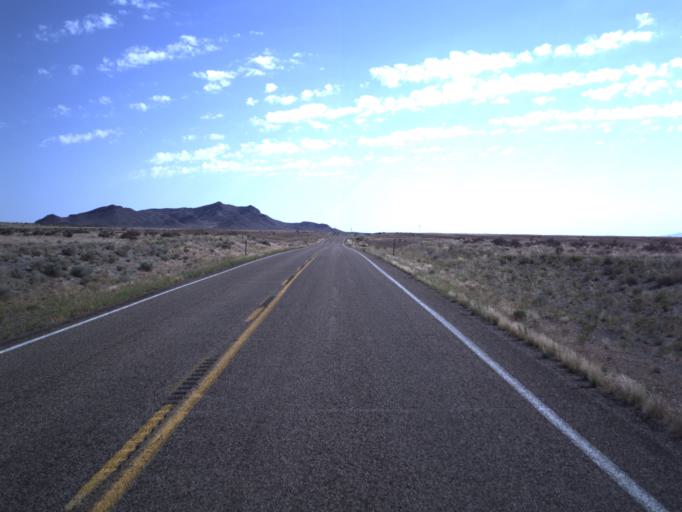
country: US
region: Utah
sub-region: Beaver County
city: Milford
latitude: 38.7824
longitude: -112.9223
